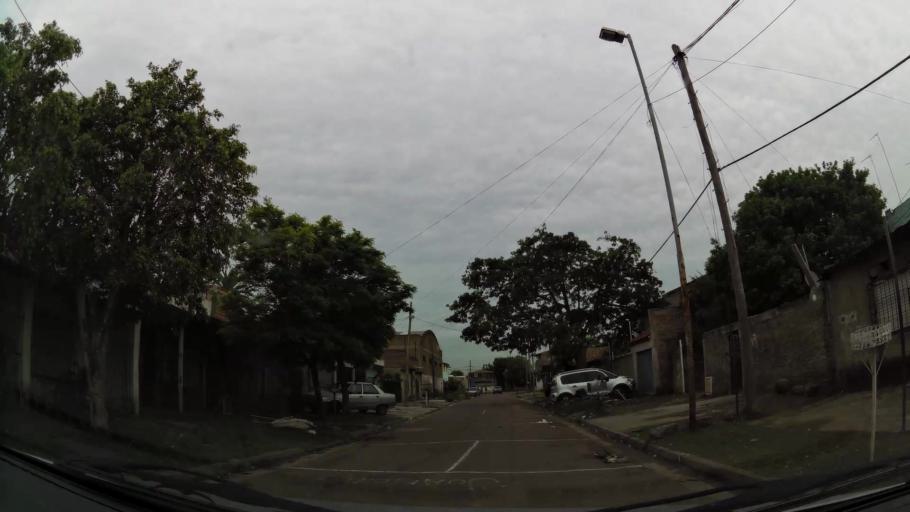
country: AR
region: Buenos Aires
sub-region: Partido de Lanus
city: Lanus
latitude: -34.7273
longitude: -58.3449
